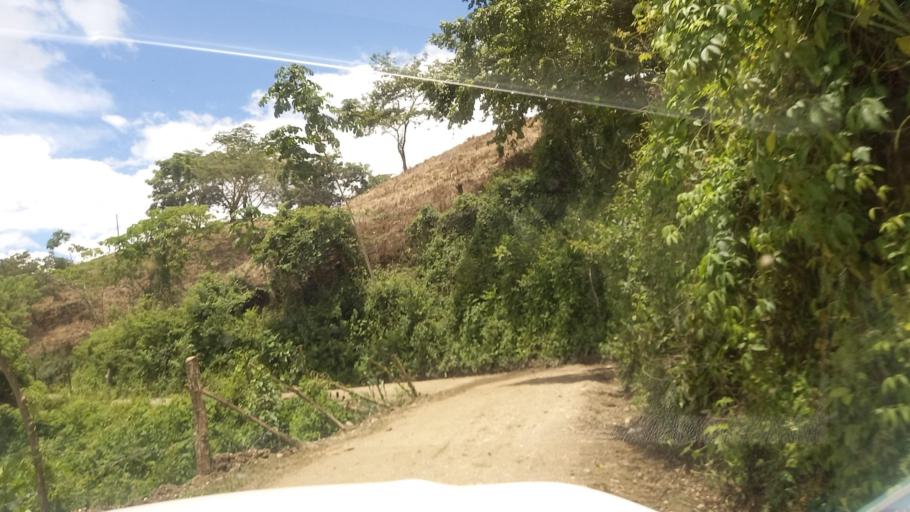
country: NI
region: Nueva Segovia
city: Wiwili
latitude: 13.7385
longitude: -85.7886
